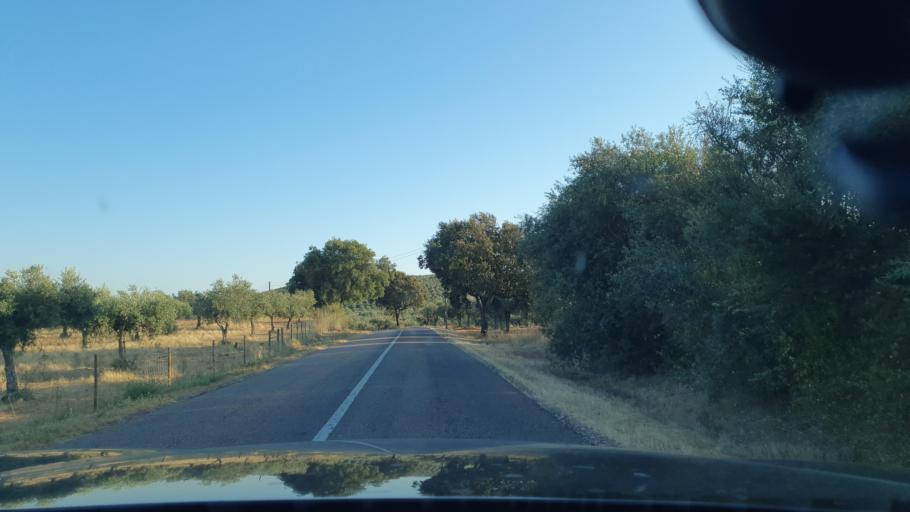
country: PT
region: Evora
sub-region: Estremoz
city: Estremoz
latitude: 38.9337
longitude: -7.6669
